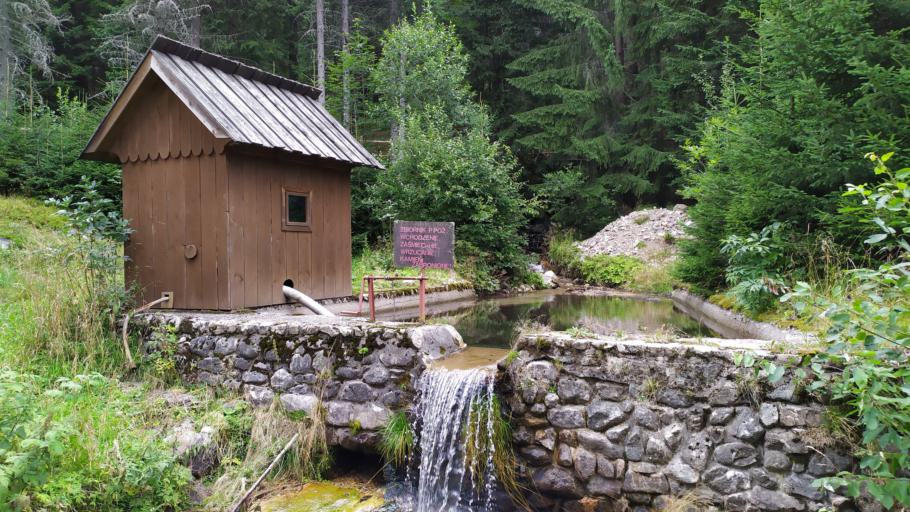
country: PL
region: Lesser Poland Voivodeship
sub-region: Powiat tatrzanski
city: Koscielisko
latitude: 49.2366
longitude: 19.7885
